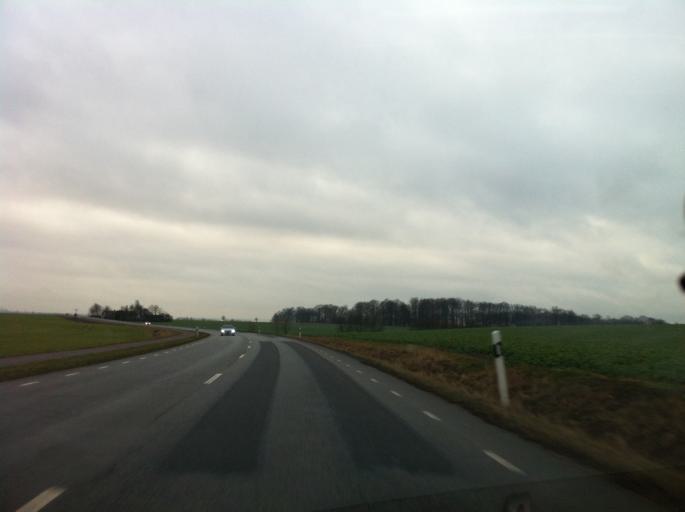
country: SE
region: Skane
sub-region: Helsingborg
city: Glumslov
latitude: 55.9270
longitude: 12.8185
